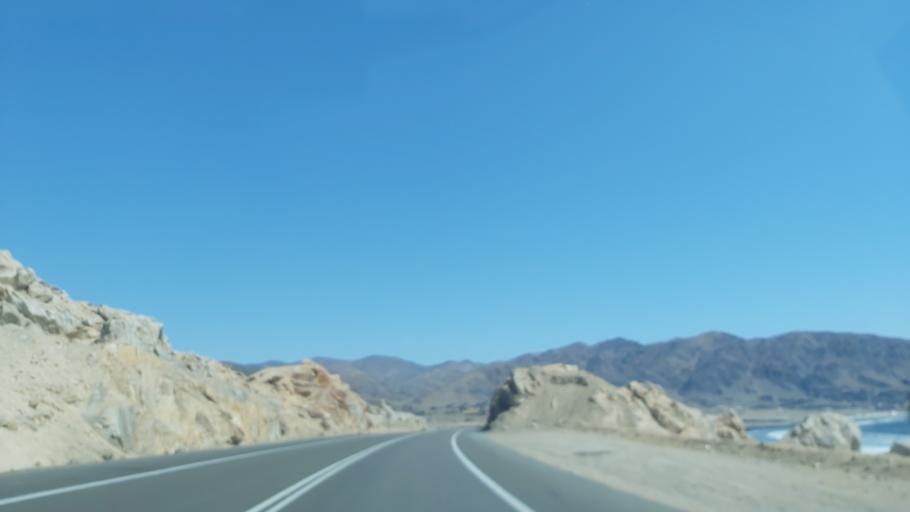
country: CL
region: Atacama
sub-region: Provincia de Chanaral
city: Diego de Almagro
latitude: -26.3796
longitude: -70.6635
